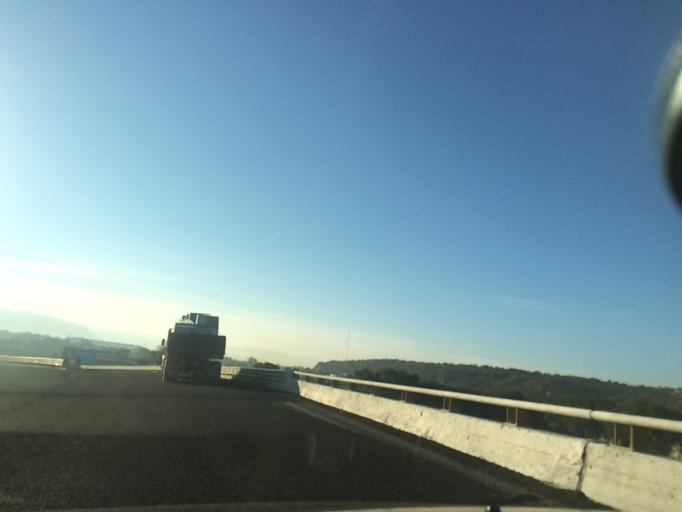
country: MX
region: Puebla
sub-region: Santiago Miahuatlan
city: San Jose Monte Chiquito
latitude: 18.4859
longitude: -97.4564
